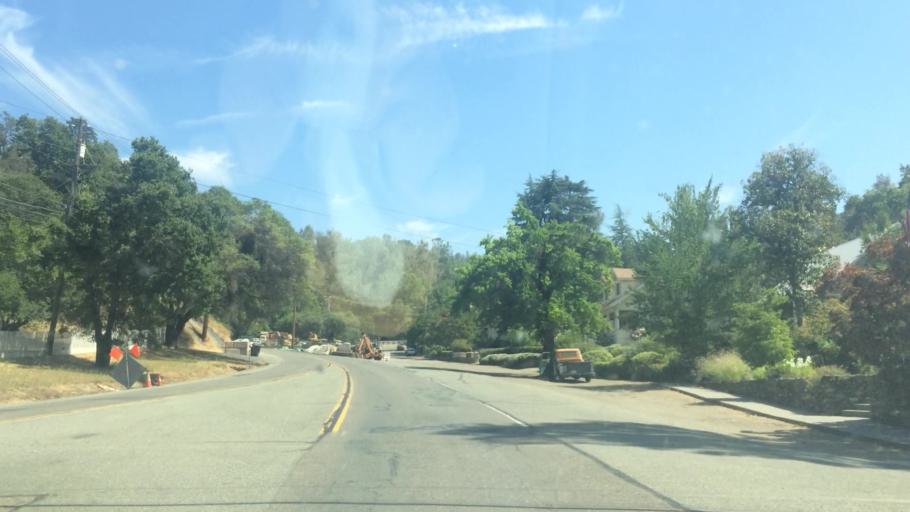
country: US
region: California
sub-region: Amador County
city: Sutter Creek
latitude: 38.3910
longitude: -120.8023
